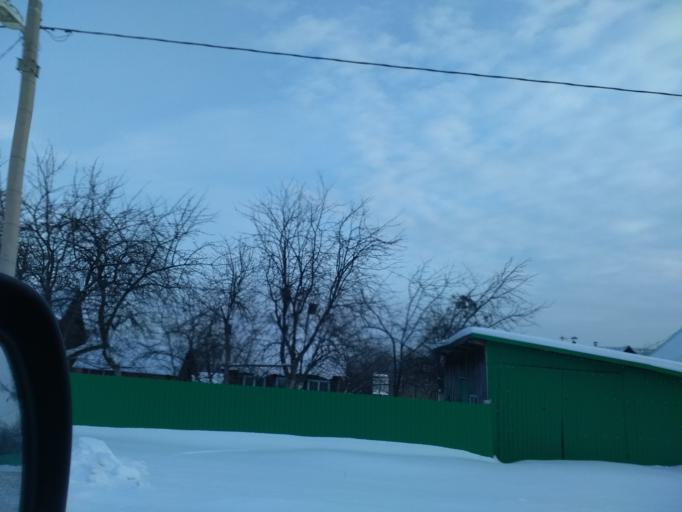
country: RU
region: Bashkortostan
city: Kudeyevskiy
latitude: 54.7381
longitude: 56.6035
